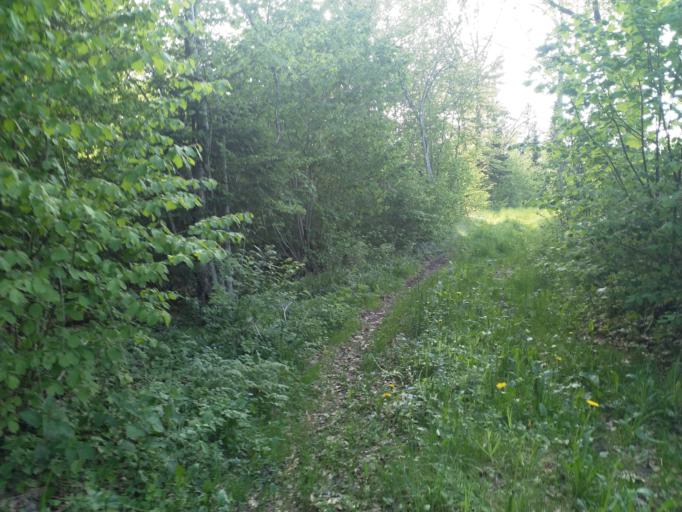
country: LV
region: Kuldigas Rajons
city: Kuldiga
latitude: 56.8556
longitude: 21.8668
